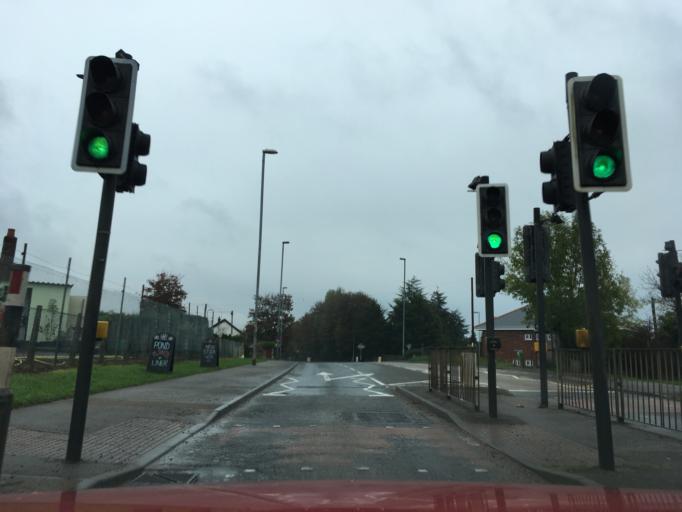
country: GB
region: Wales
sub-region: Newport
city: Langstone
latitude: 51.6082
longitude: -2.8952
